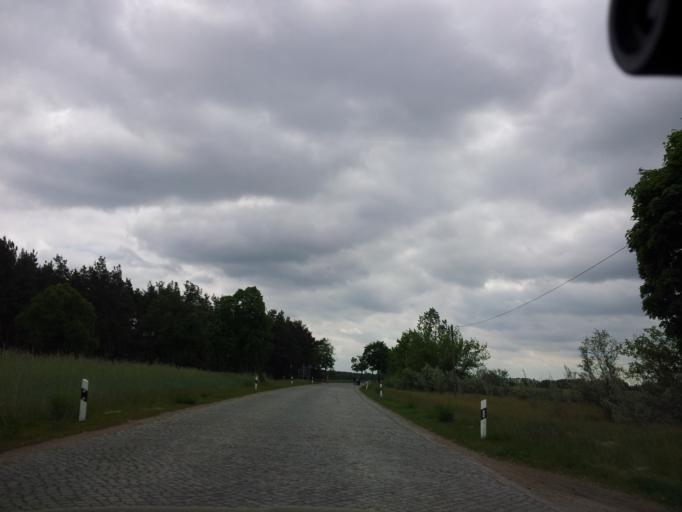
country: DE
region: Brandenburg
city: Beelitz
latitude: 52.1355
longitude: 12.9890
